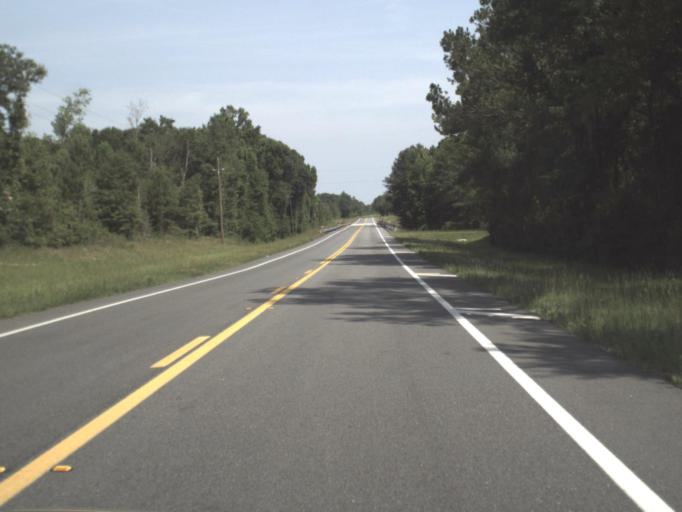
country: US
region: Georgia
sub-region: Echols County
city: Statenville
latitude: 30.6018
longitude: -83.0149
